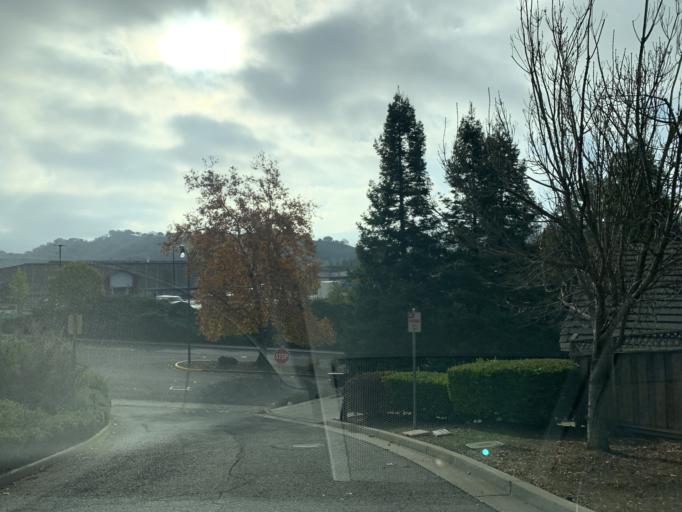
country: US
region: California
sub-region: Contra Costa County
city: Saranap
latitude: 37.8801
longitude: -122.0741
